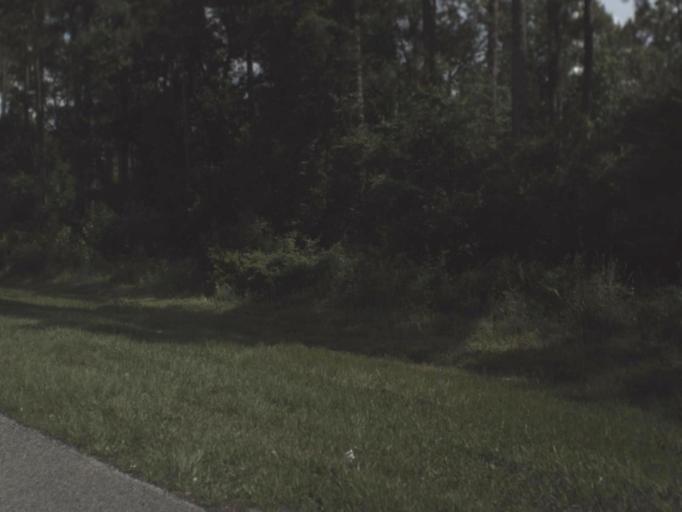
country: US
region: Florida
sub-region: Alachua County
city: Alachua
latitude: 29.7269
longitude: -82.3716
